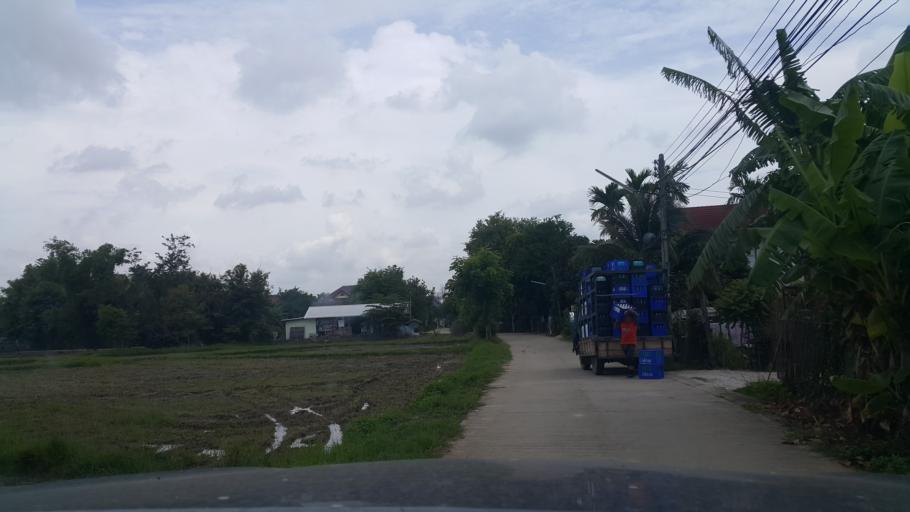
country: TH
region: Lamphun
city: Ban Thi
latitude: 18.6697
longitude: 99.1508
